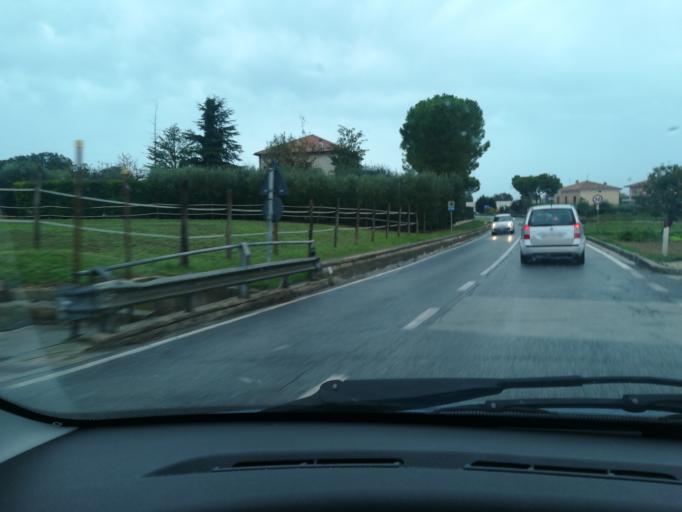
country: IT
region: The Marches
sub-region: Provincia di Macerata
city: Santa Maria Apparente
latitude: 43.2943
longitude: 13.6749
